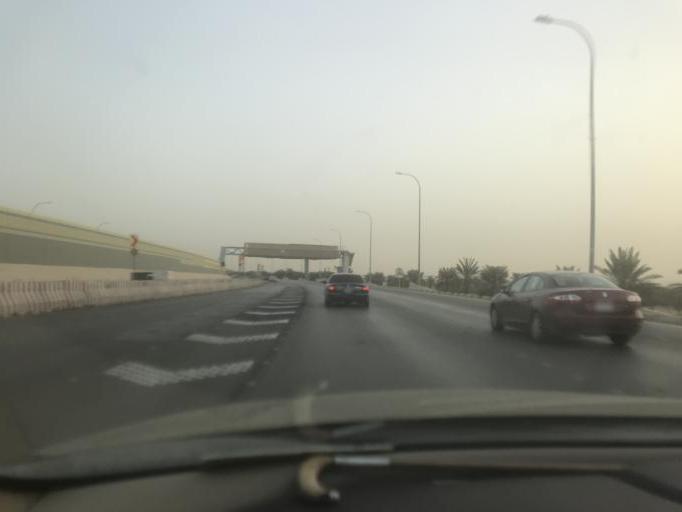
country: SA
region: Ar Riyad
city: Riyadh
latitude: 24.9122
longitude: 46.7227
